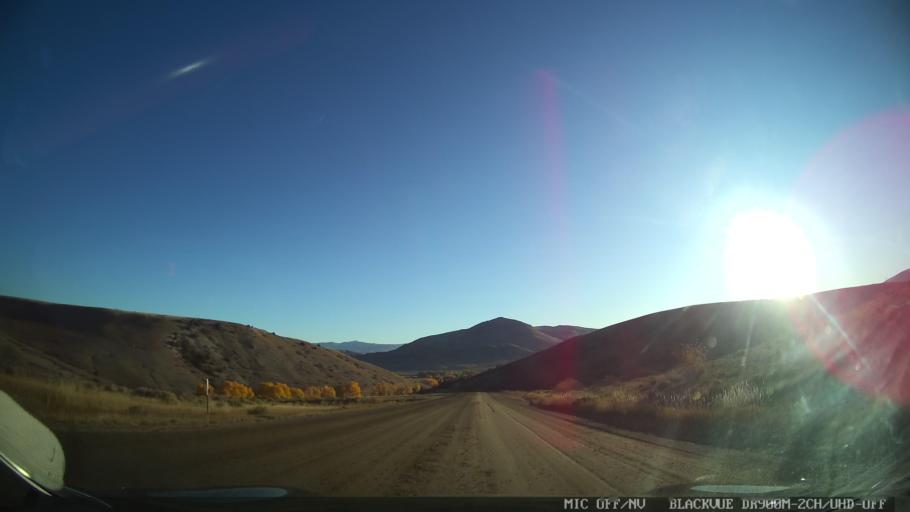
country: US
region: Colorado
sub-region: Grand County
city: Kremmling
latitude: 40.0131
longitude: -106.3981
